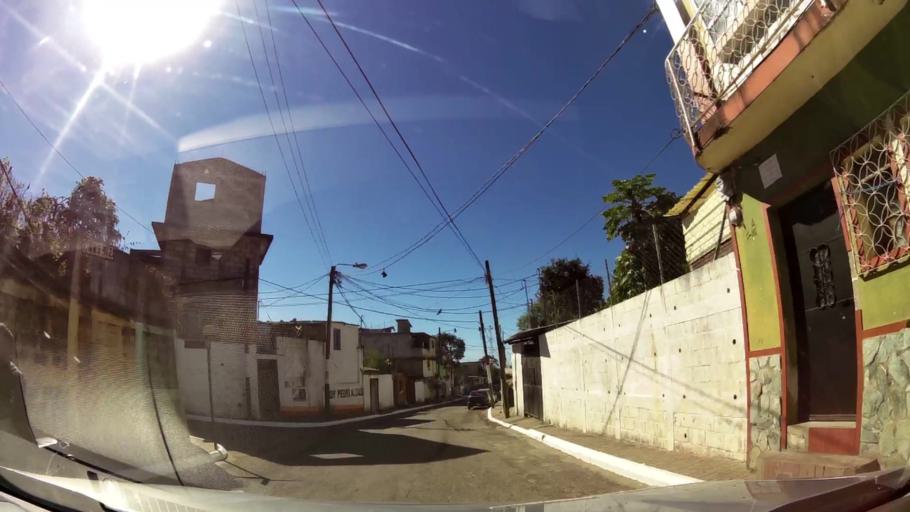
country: GT
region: Guatemala
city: Fraijanes
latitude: 14.4611
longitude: -90.4403
